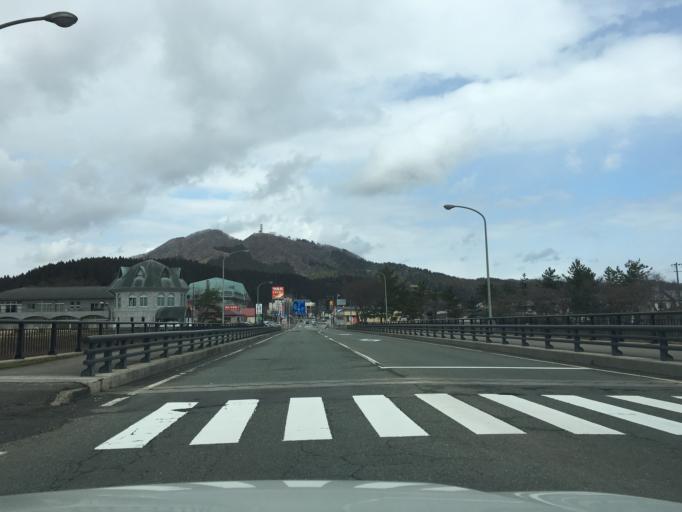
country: JP
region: Akita
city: Tenno
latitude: 39.9406
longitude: 140.1120
